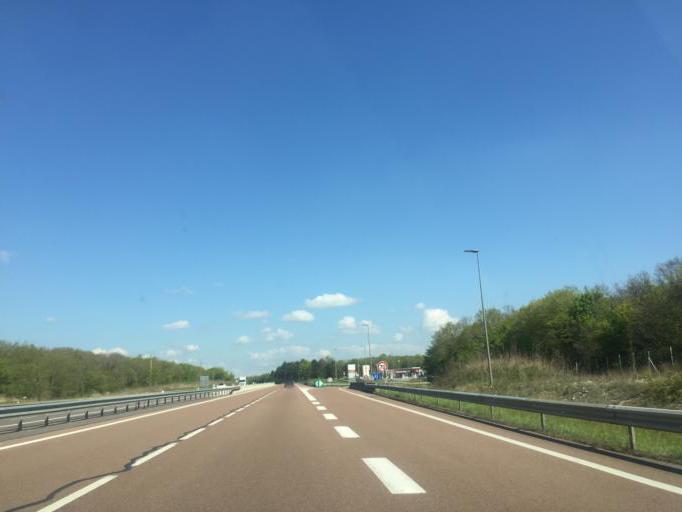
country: FR
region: Bourgogne
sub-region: Departement de la Cote-d'Or
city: Savigny-les-Beaune
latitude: 47.1097
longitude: 4.7127
